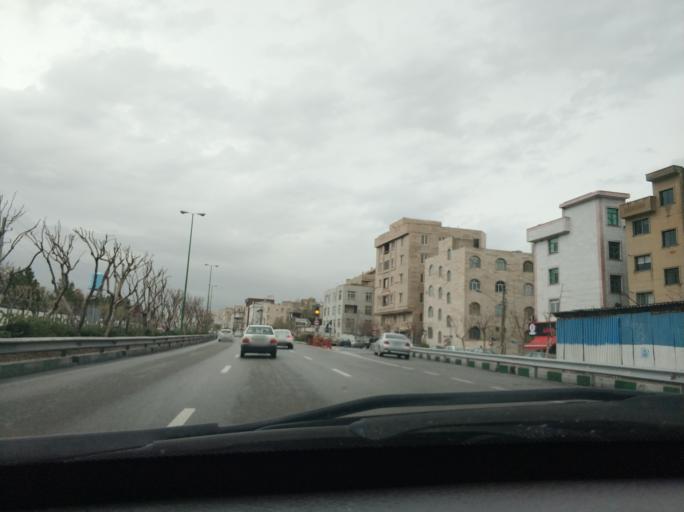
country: IR
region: Tehran
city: Tehran
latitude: 35.7102
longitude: 51.4439
